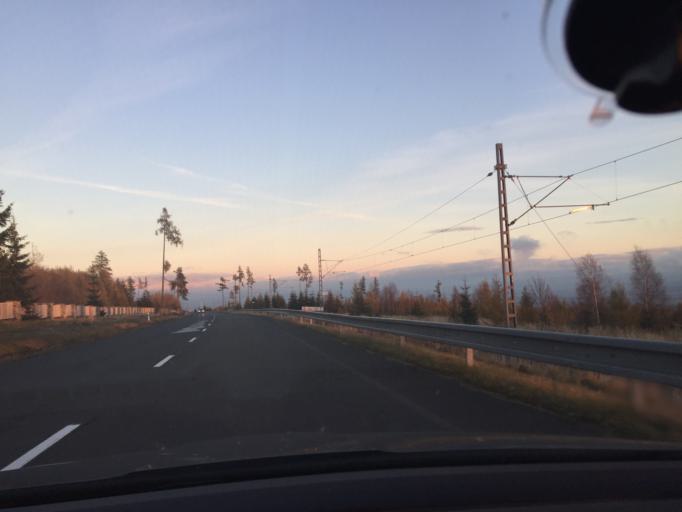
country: SK
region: Presovsky
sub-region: Okres Poprad
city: Svit
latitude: 49.1176
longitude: 20.1546
